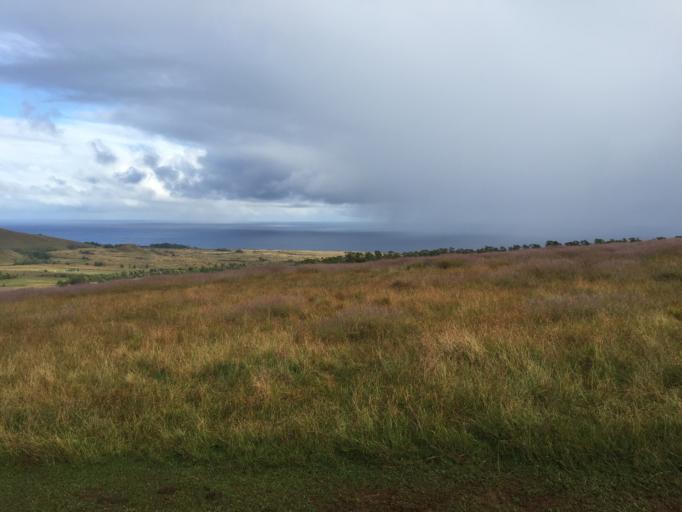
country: CL
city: Ostrov Paskhi
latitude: -27.1126
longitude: -109.3831
